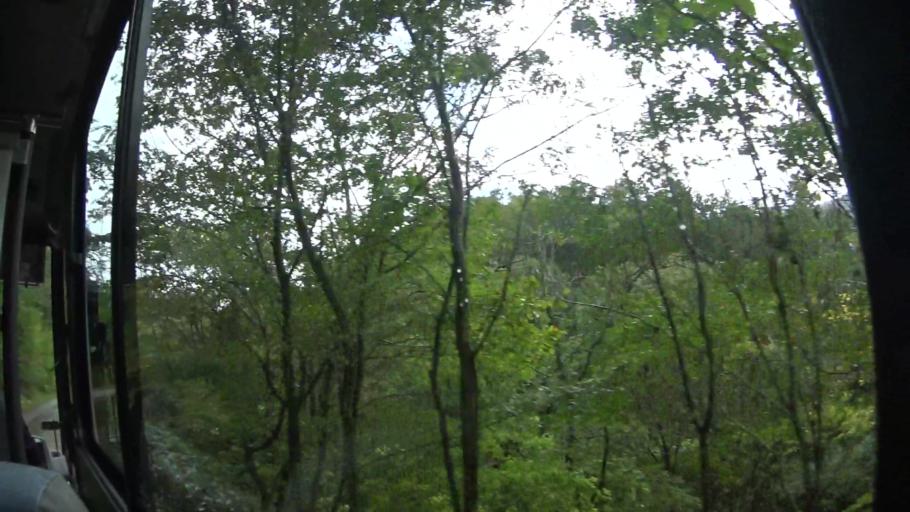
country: JP
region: Kyoto
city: Miyazu
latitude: 35.5882
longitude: 135.1905
